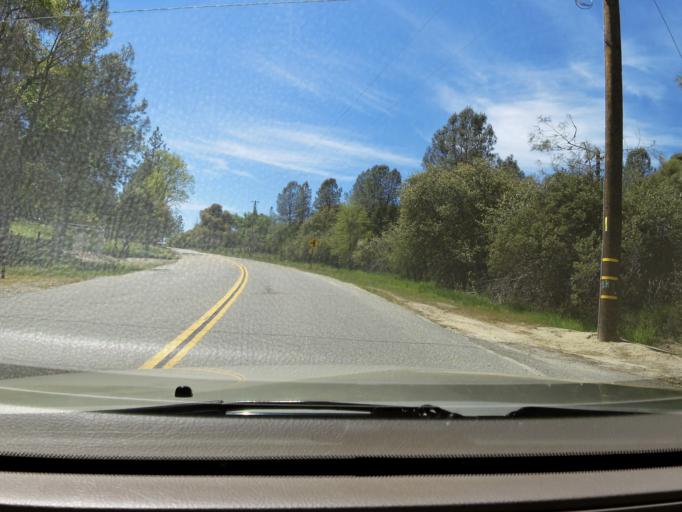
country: US
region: California
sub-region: Madera County
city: Oakhurst
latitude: 37.2426
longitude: -119.5259
